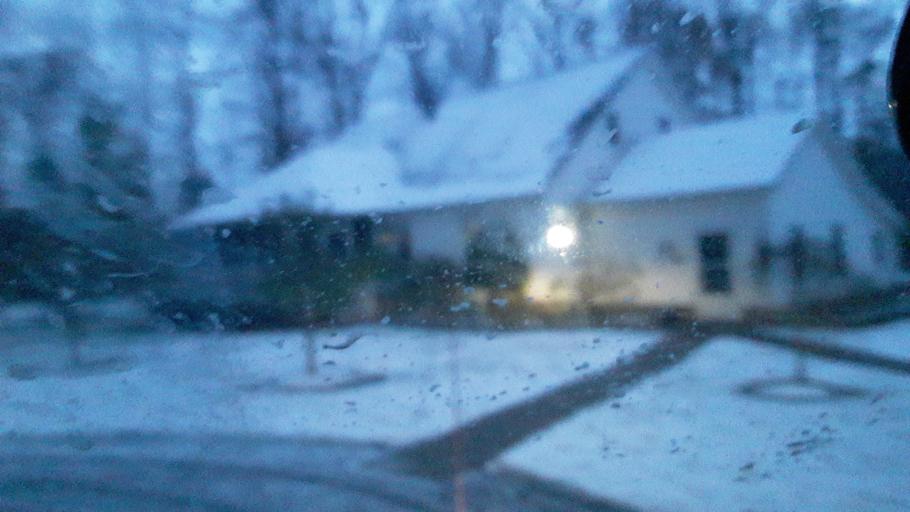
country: US
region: Ohio
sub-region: Portage County
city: Hiram
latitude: 41.3628
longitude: -81.1517
